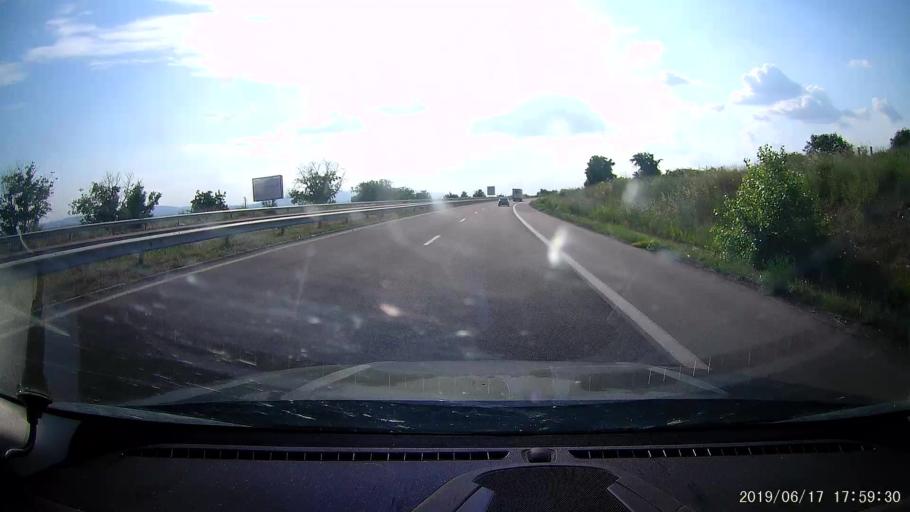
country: BG
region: Khaskovo
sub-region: Obshtina Svilengrad
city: Svilengrad
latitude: 41.7246
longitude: 26.2966
